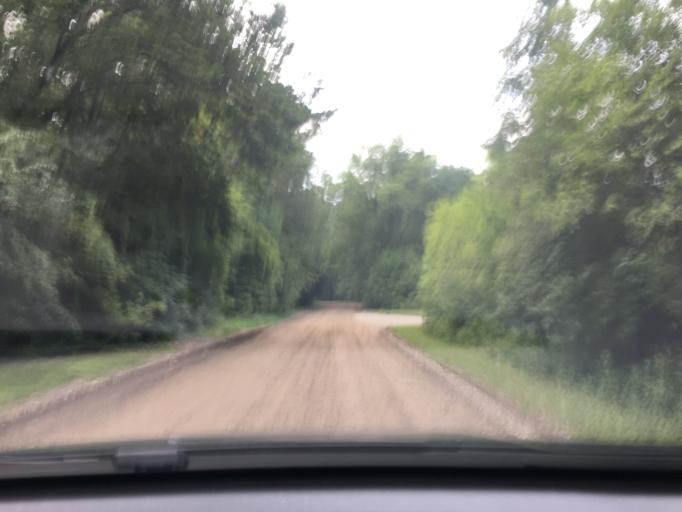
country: US
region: Michigan
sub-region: Oakland County
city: Bloomfield Hills
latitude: 42.5798
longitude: -83.2309
